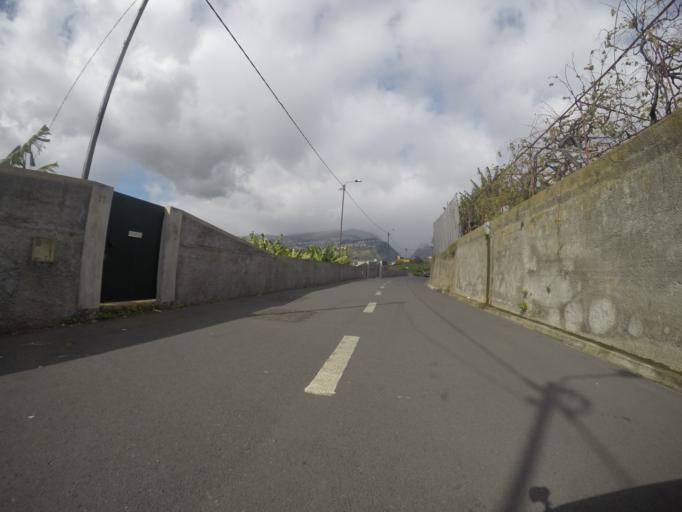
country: PT
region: Madeira
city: Camara de Lobos
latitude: 32.6489
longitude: -16.9517
